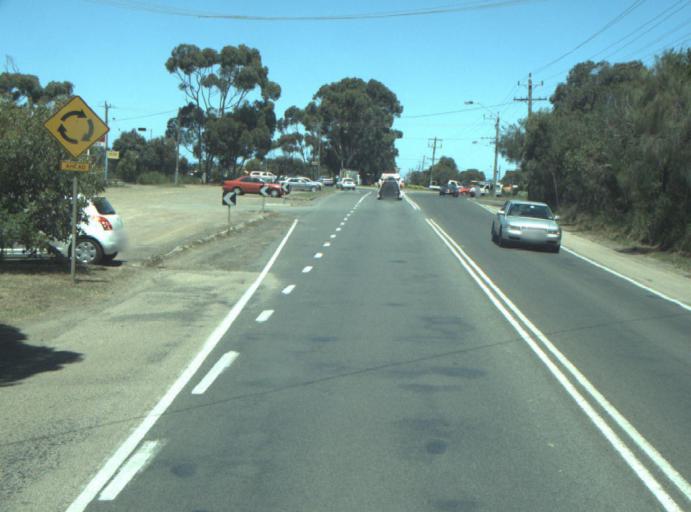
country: AU
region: Victoria
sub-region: Greater Geelong
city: Leopold
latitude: -38.2562
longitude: 144.5359
